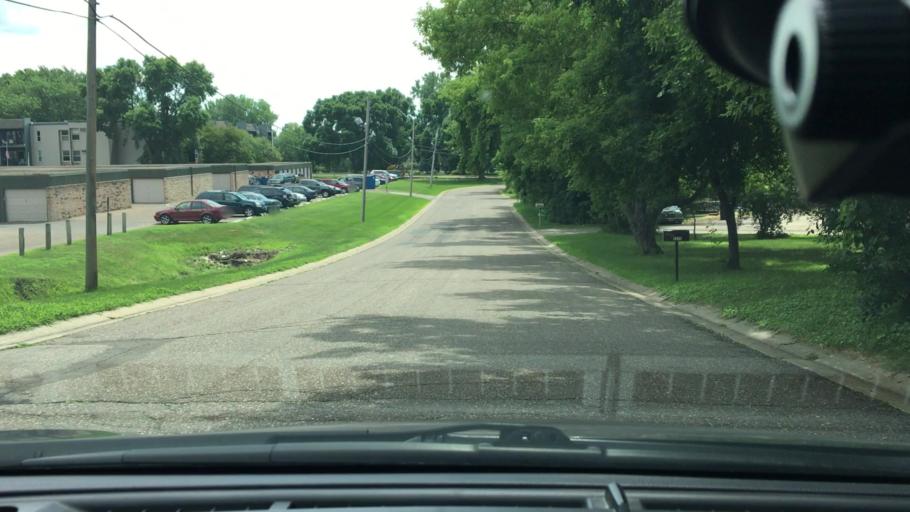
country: US
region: Minnesota
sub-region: Hennepin County
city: New Hope
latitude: 45.0071
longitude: -93.4057
